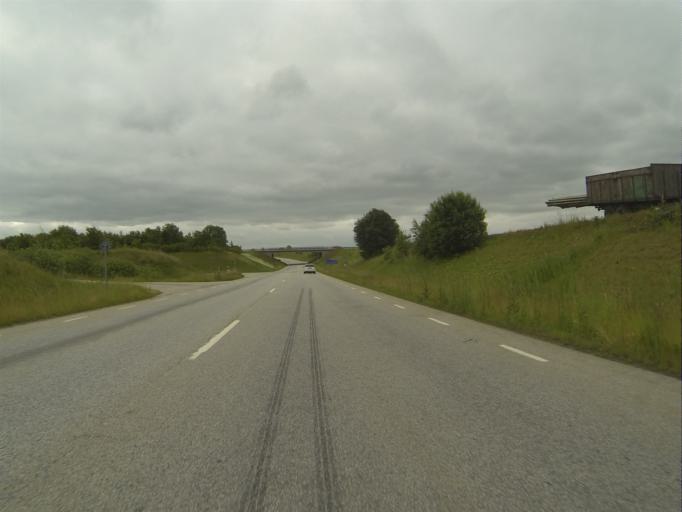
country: SE
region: Skane
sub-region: Svedala Kommun
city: Klagerup
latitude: 55.6453
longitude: 13.2659
